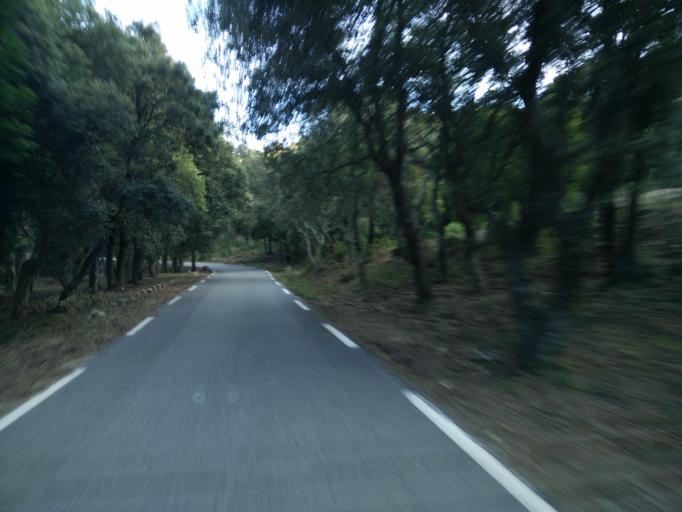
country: FR
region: Provence-Alpes-Cote d'Azur
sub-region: Departement du Var
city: Bormes-les-Mimosas
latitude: 43.1876
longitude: 6.3251
